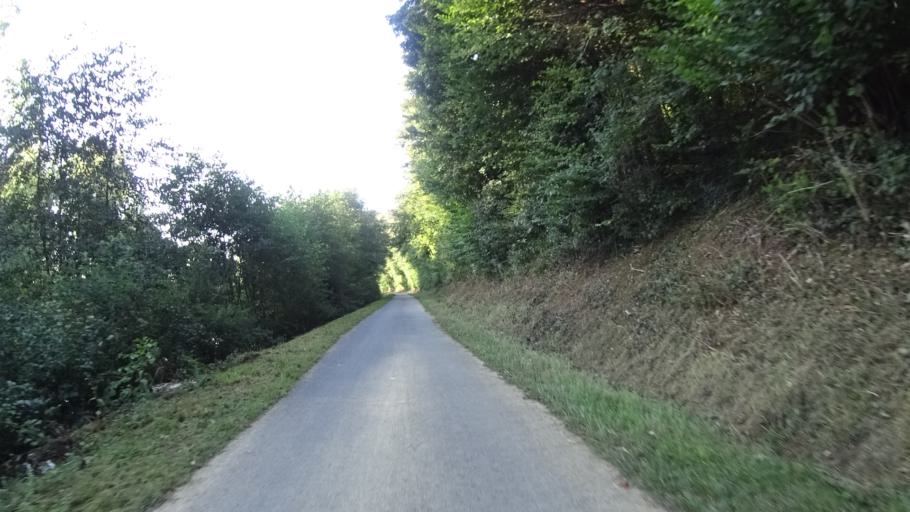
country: FR
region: Franche-Comte
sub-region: Territoire de Belfort
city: Mezire
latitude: 47.5431
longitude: 6.9067
